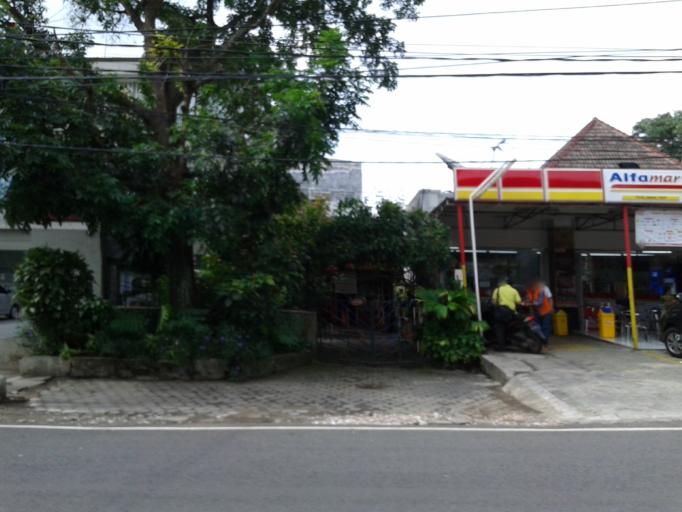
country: ID
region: East Java
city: Malang
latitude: -7.9654
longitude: 112.6174
